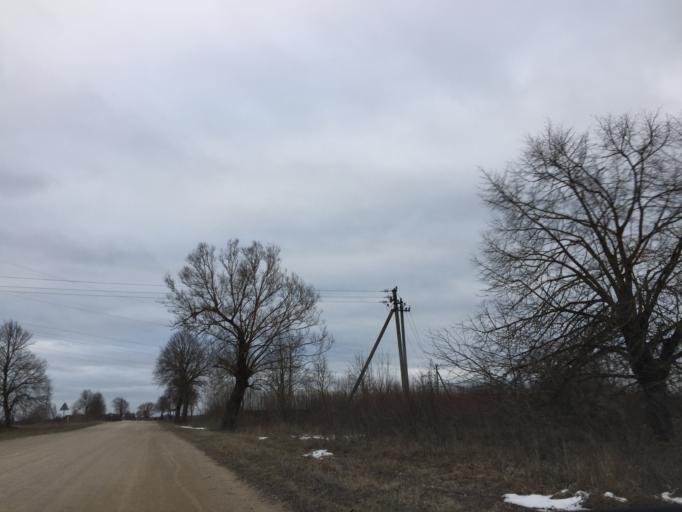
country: LT
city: Zagare
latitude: 56.3493
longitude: 23.2534
